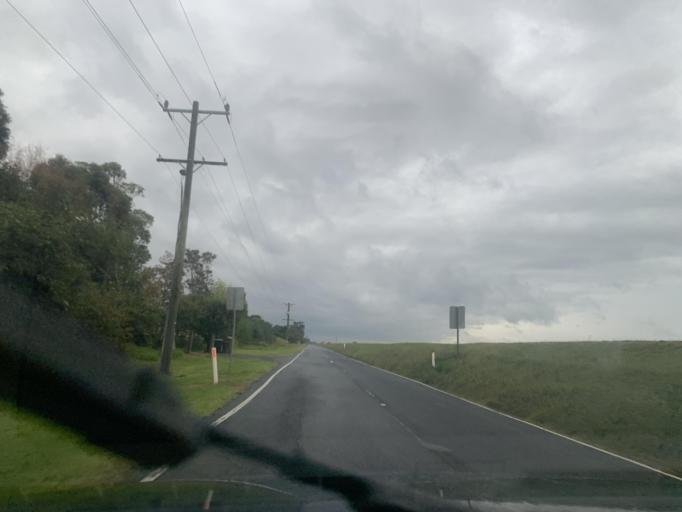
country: AU
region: Victoria
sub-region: Kingston
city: Chelsea Heights
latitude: -38.0277
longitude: 145.1595
